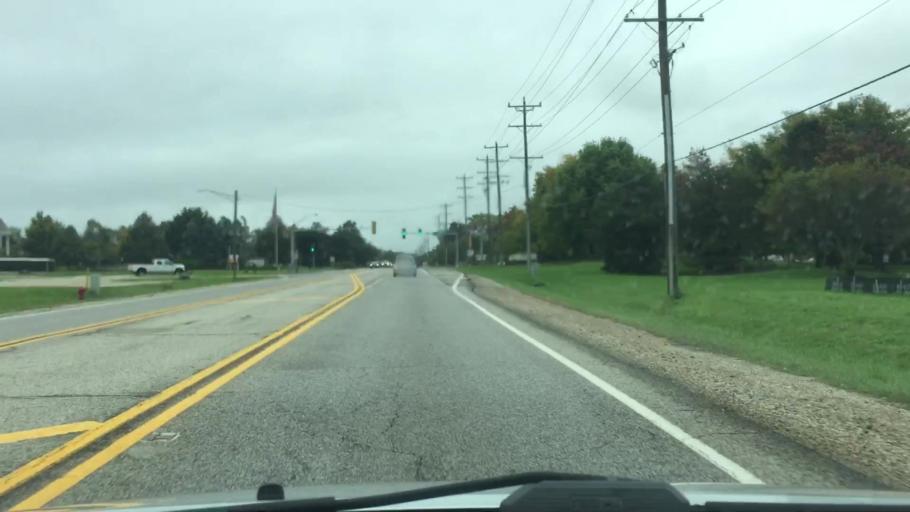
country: US
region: Illinois
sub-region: McHenry County
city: McHenry
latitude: 42.3096
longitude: -88.2802
